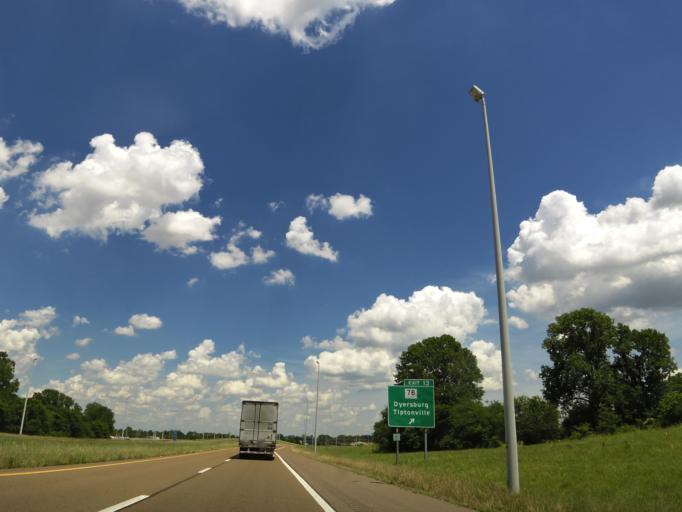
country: US
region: Tennessee
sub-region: Dyer County
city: Dyersburg
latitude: 36.0687
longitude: -89.4039
